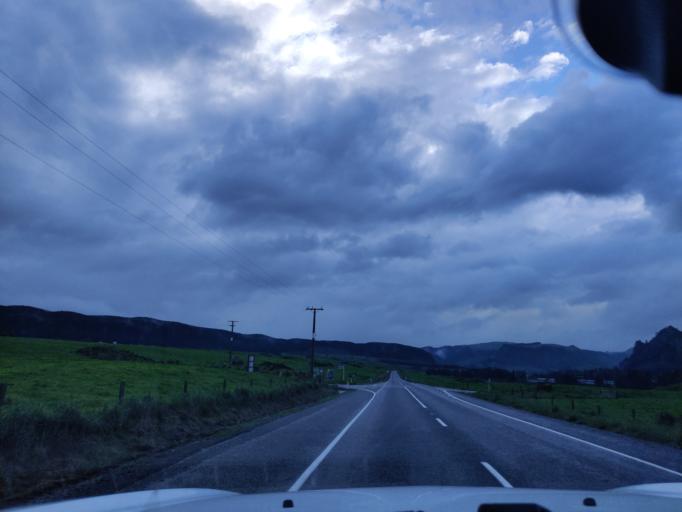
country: NZ
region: Waikato
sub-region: South Waikato District
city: Tokoroa
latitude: -38.4081
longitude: 175.7961
